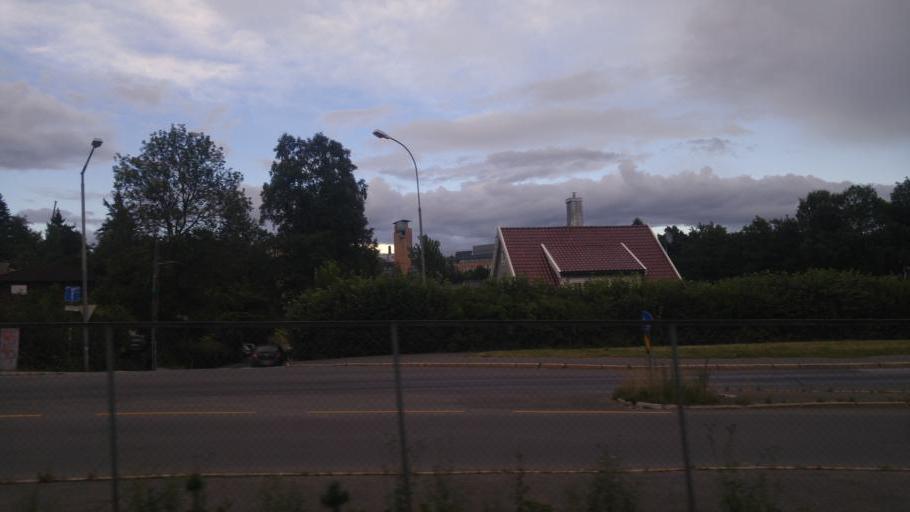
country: NO
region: Oslo
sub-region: Oslo
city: Sjolyststranda
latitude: 59.9470
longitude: 10.7103
